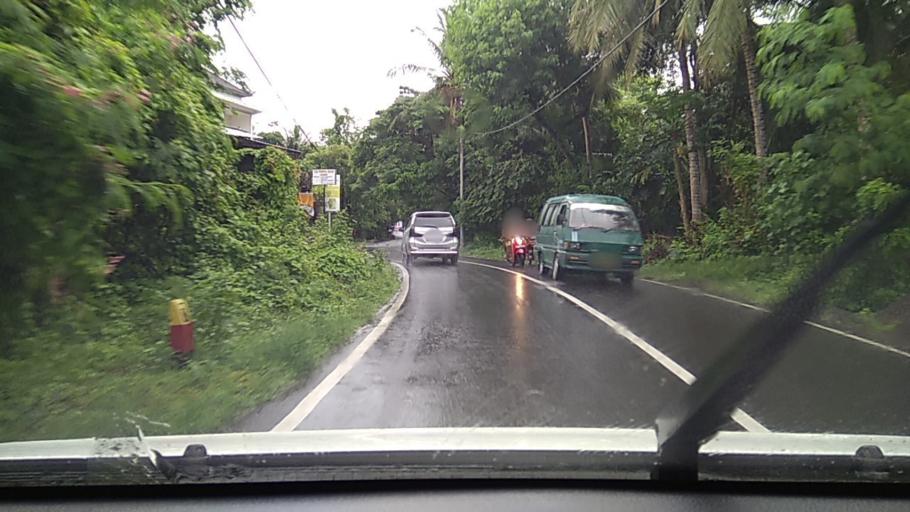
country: ID
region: Bali
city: Banjar Danginsema
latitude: -8.4699
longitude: 115.6195
